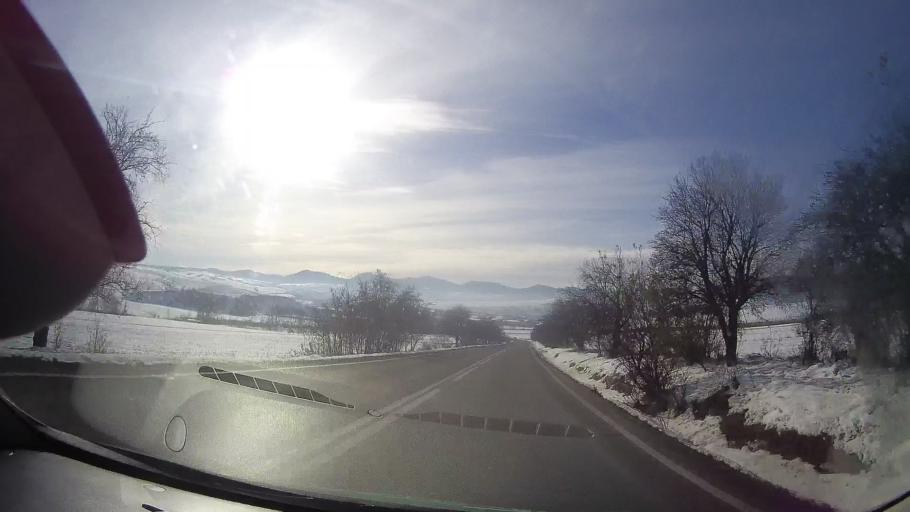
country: RO
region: Neamt
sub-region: Comuna Baltatesti
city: Valea Seaca
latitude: 47.1484
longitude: 26.3238
